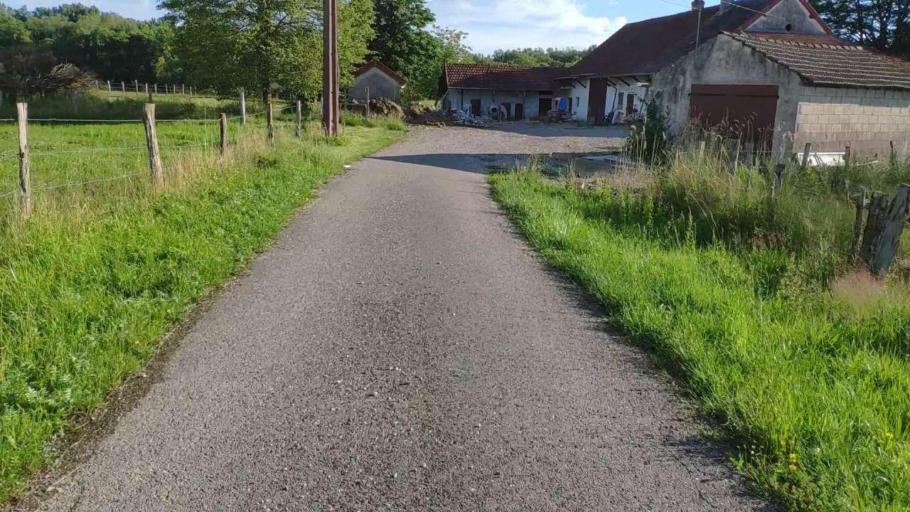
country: FR
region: Franche-Comte
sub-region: Departement du Jura
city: Bletterans
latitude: 46.7812
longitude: 5.4796
